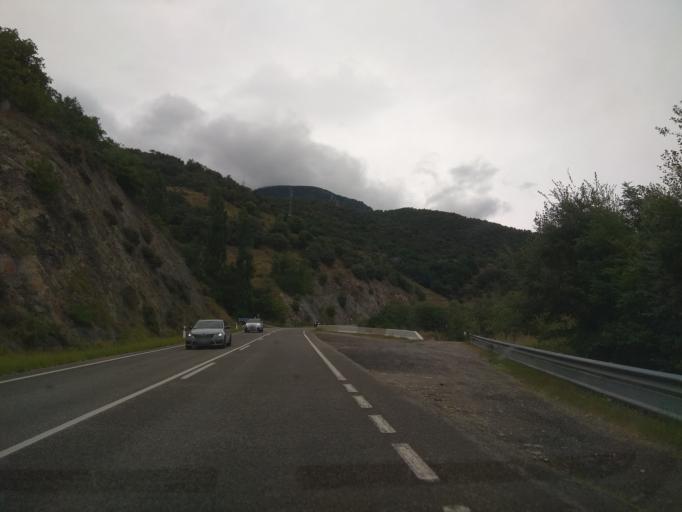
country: ES
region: Catalonia
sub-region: Provincia de Lleida
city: el Pont de Bar
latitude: 42.3603
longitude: 1.5699
